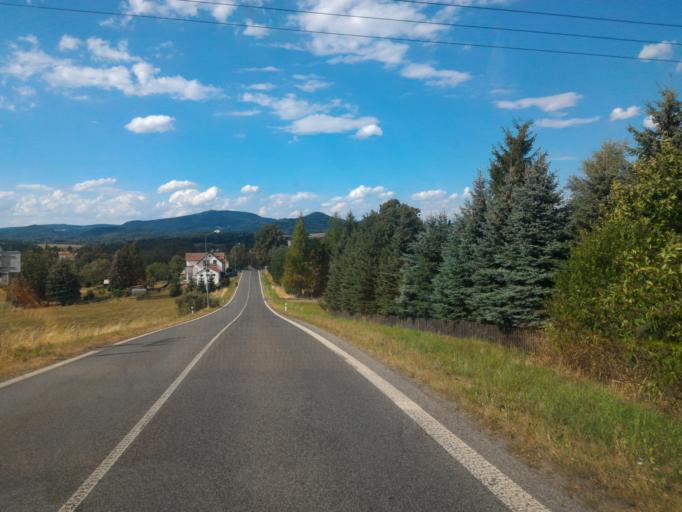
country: CZ
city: Jablonne v Podjestedi
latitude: 50.7563
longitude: 14.7607
